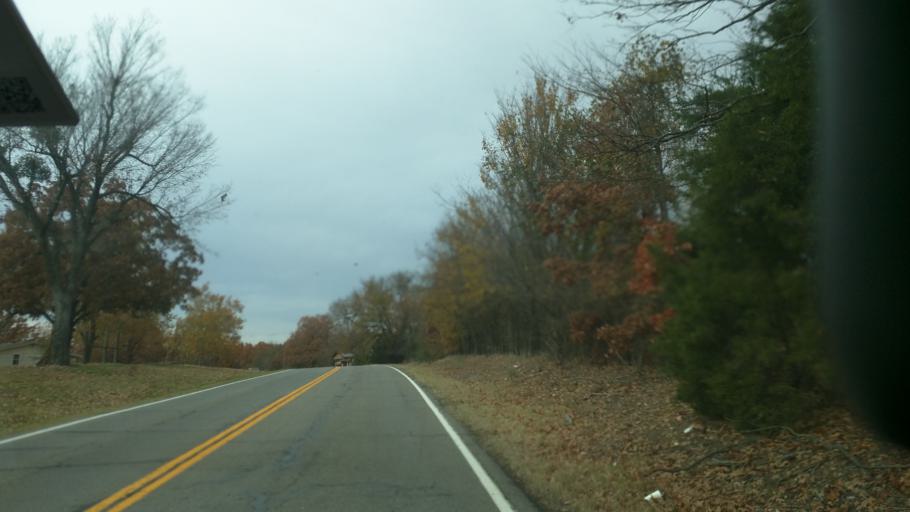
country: US
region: Oklahoma
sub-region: Cherokee County
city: Tahlequah
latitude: 35.9283
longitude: -94.8520
